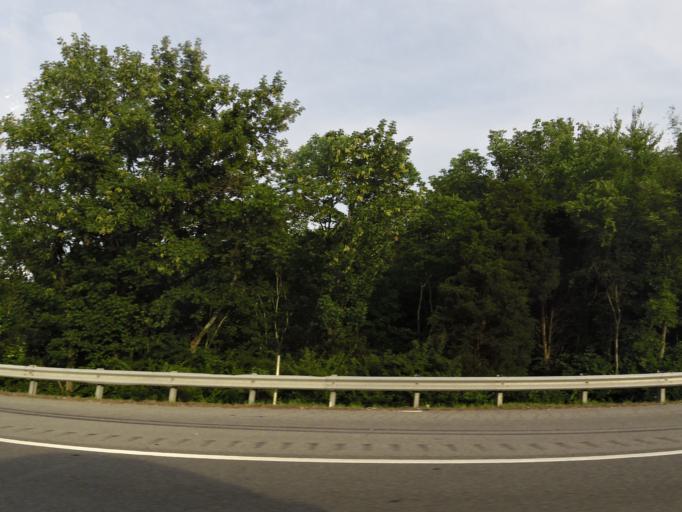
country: US
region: Tennessee
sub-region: Davidson County
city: Belle Meade
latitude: 36.1059
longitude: -86.9298
